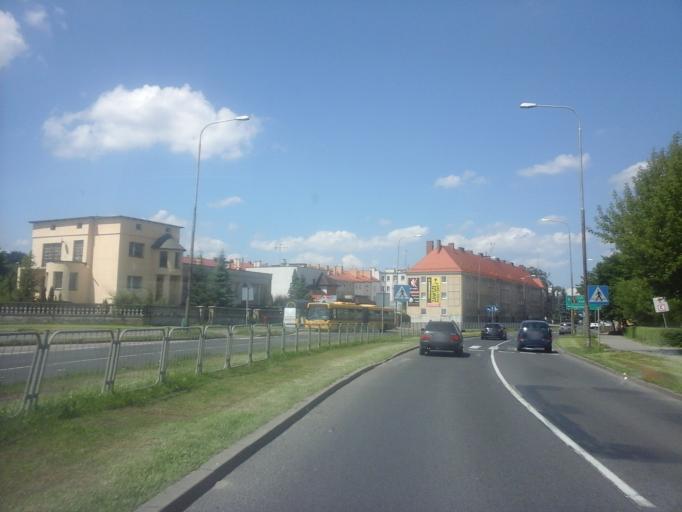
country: PL
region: West Pomeranian Voivodeship
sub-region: Koszalin
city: Koszalin
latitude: 54.1835
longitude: 16.1799
